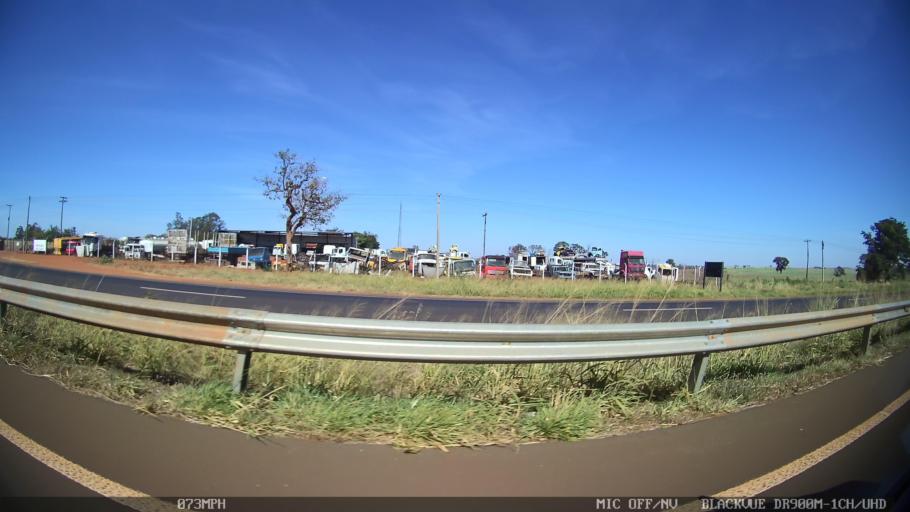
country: BR
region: Sao Paulo
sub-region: Barretos
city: Barretos
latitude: -20.5432
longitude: -48.6201
